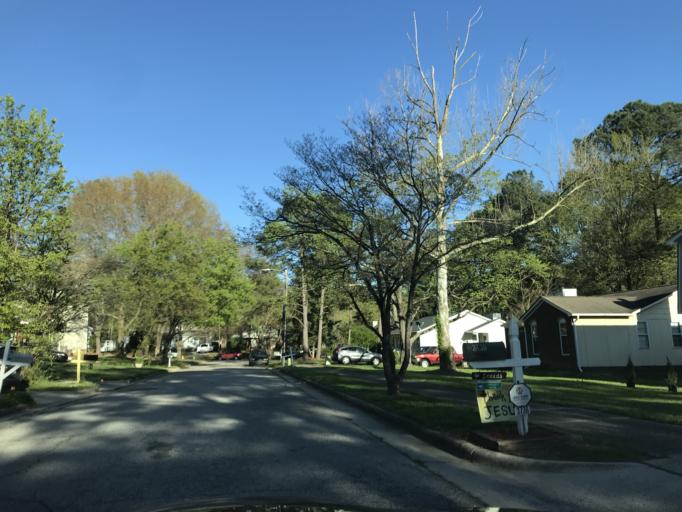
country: US
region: North Carolina
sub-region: Wake County
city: Raleigh
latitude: 35.8337
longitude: -78.5757
